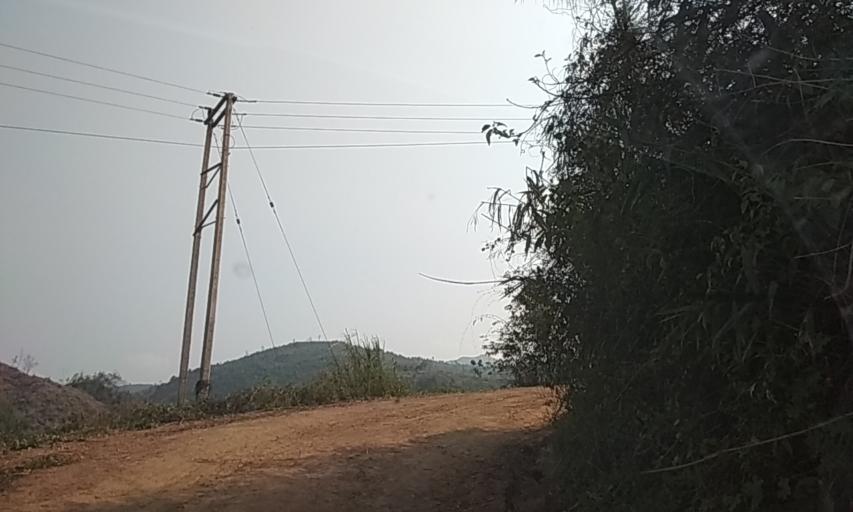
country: LA
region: Louangphabang
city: Louangphabang
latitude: 20.0419
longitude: 101.8355
